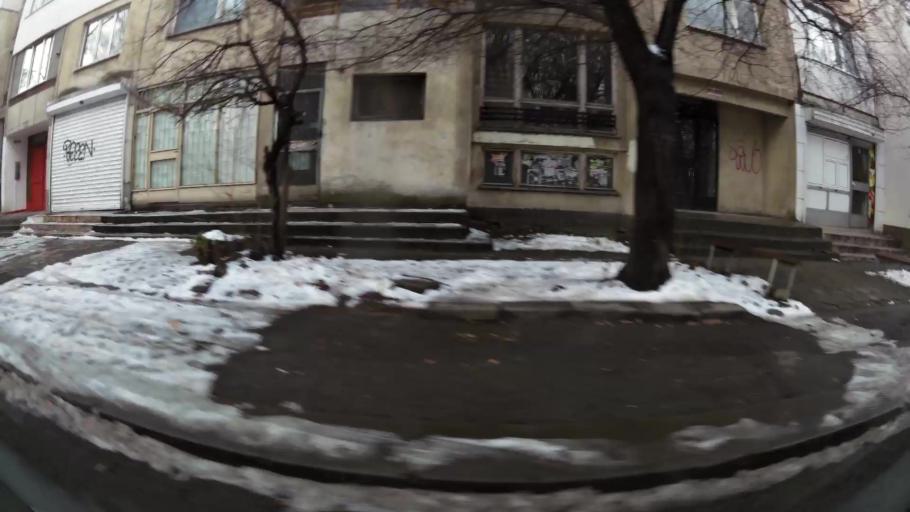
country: BG
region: Sofia-Capital
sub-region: Stolichna Obshtina
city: Sofia
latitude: 42.6966
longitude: 23.2915
